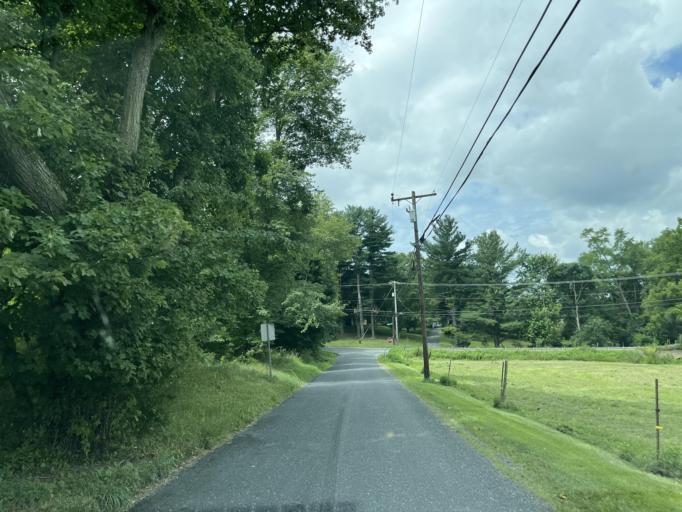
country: US
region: Maryland
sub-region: Montgomery County
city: Montgomery Village
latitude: 39.2282
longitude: -77.1766
